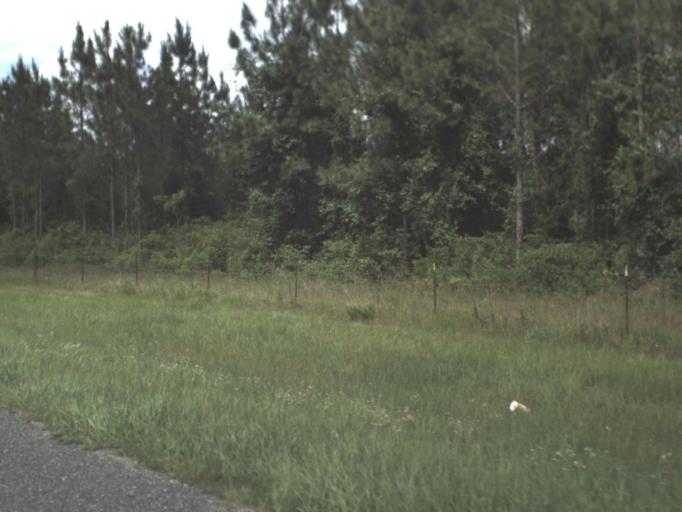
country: US
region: Florida
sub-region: Clay County
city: Middleburg
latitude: 29.9945
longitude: -81.8977
